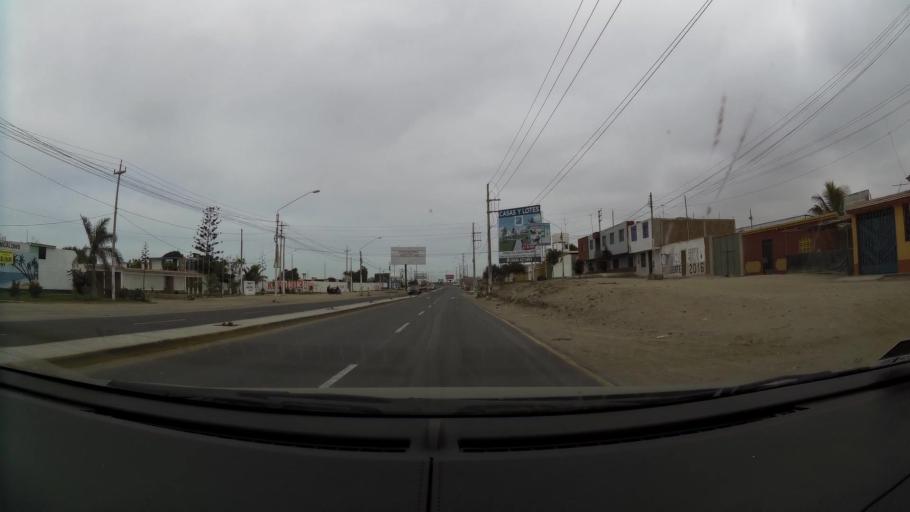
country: PE
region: La Libertad
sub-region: Provincia de Trujillo
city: Huanchaco
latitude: -8.0886
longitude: -79.0931
